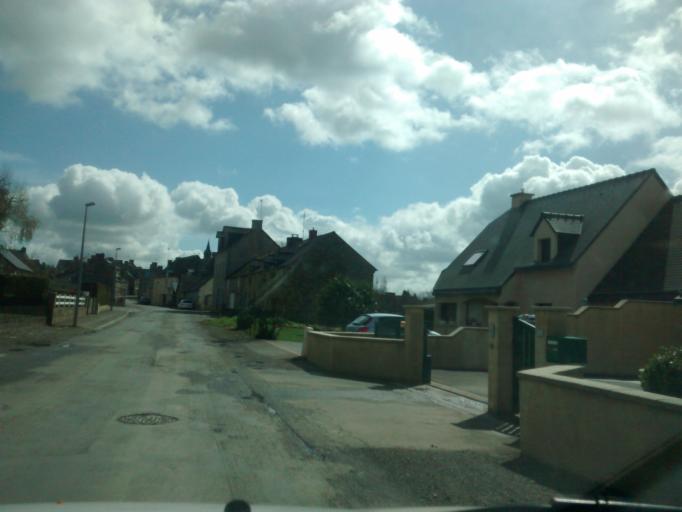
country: FR
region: Brittany
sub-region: Departement d'Ille-et-Vilaine
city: Livre-sur-Changeon
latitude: 48.1932
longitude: -1.3730
